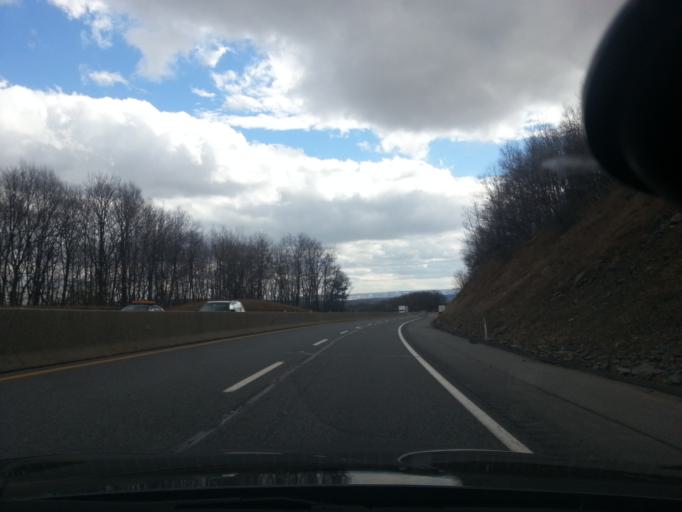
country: US
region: Pennsylvania
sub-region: Carbon County
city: Weissport East
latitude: 40.9009
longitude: -75.6386
